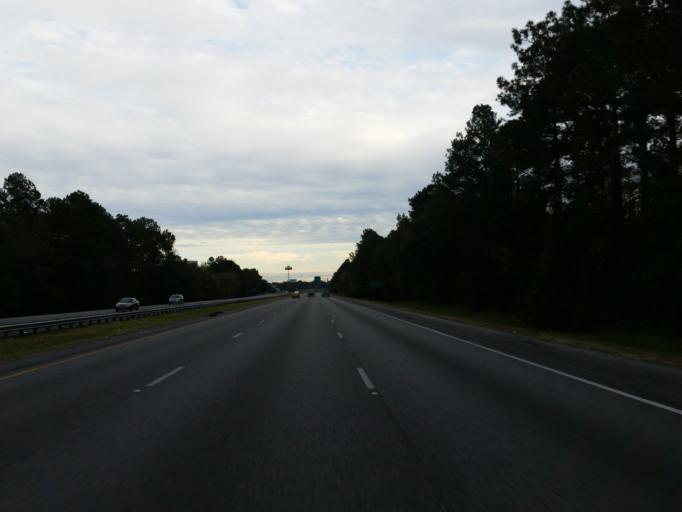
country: US
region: Georgia
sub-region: Lowndes County
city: Valdosta
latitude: 30.7627
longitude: -83.2836
